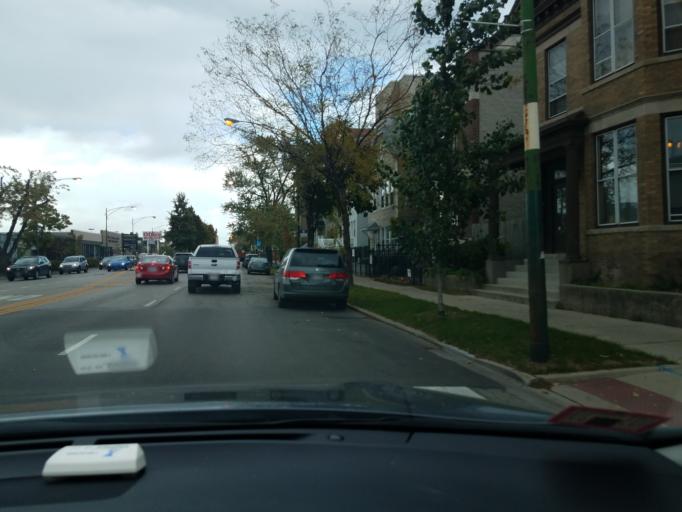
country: US
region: Illinois
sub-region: Cook County
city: Chicago
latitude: 41.9333
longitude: -87.6683
